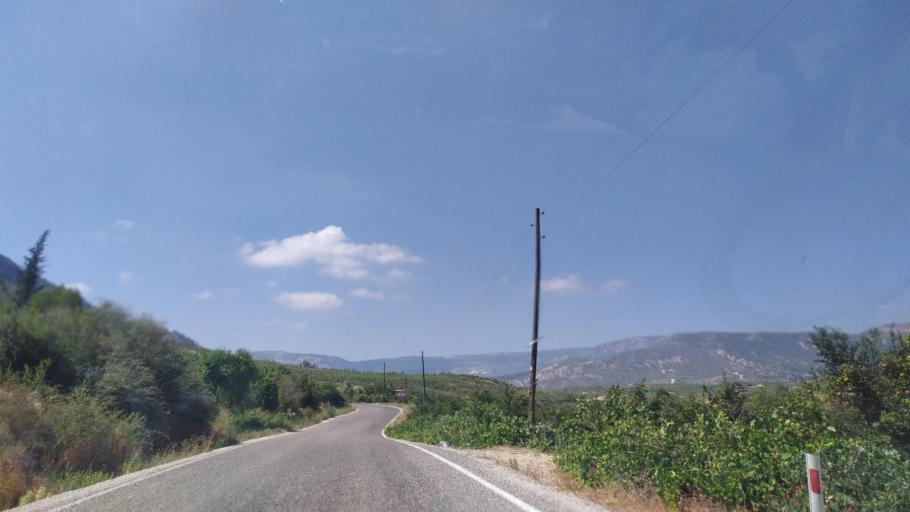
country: TR
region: Mersin
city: Ovacik
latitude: 36.2413
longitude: 33.5364
